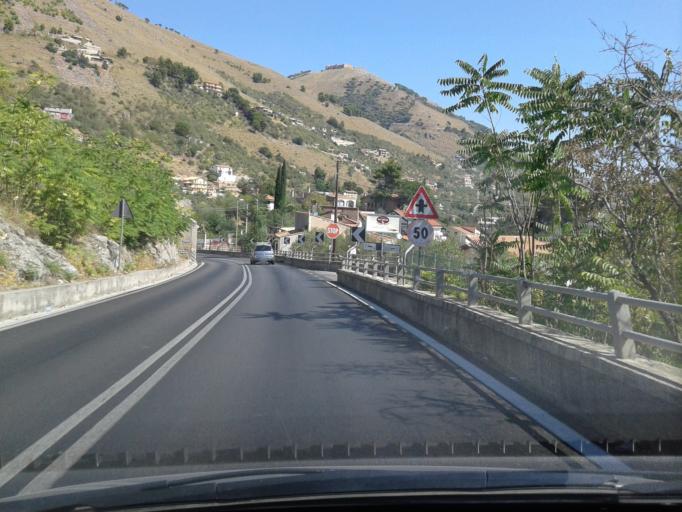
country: IT
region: Sicily
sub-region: Palermo
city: Cannizzaro-Favara
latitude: 38.0675
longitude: 13.2695
